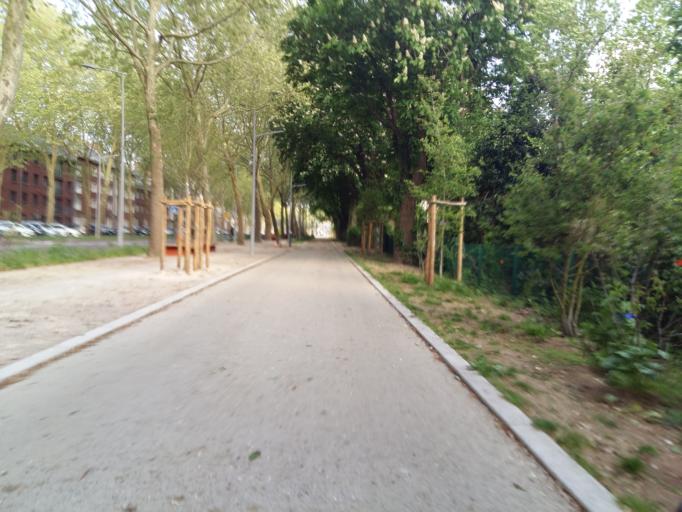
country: FR
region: Picardie
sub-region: Departement de la Somme
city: Amiens
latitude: 49.8920
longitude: 2.2874
